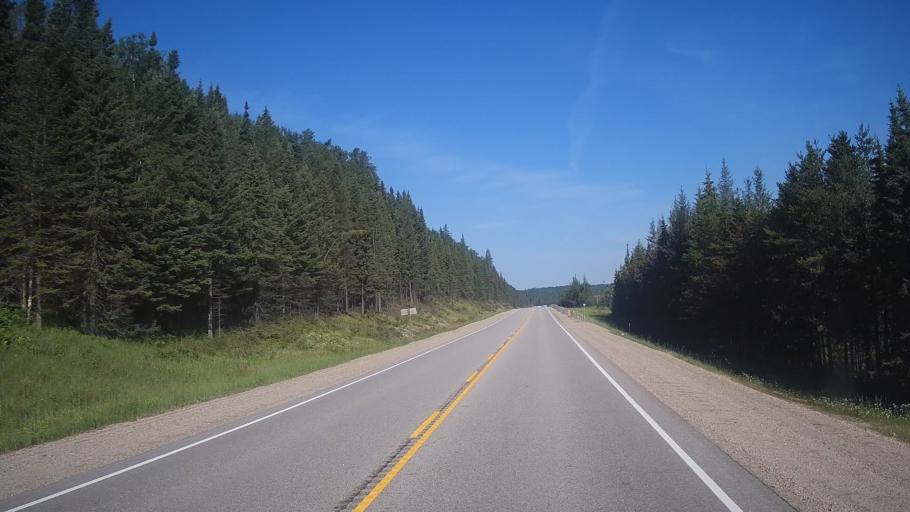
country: CA
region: Ontario
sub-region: Rainy River District
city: Atikokan
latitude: 49.4678
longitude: -91.9187
